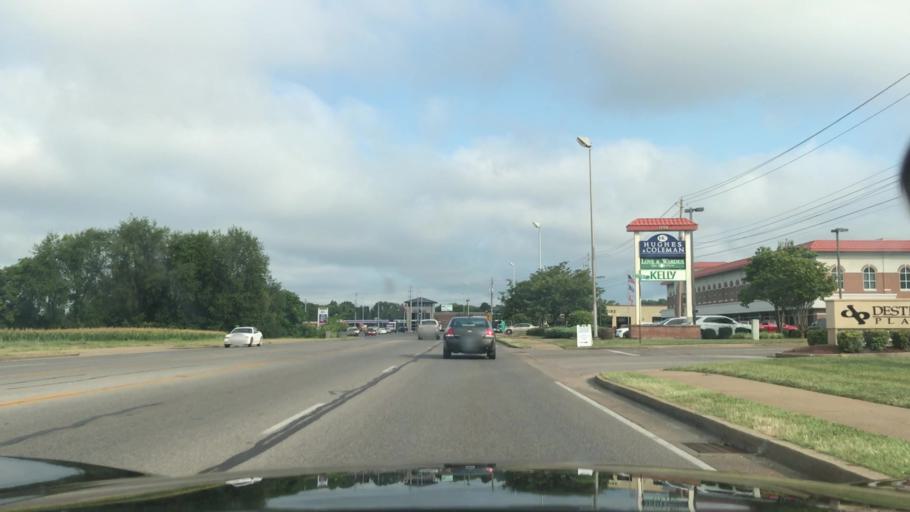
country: US
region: Kentucky
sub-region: Warren County
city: Bowling Green
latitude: 36.9588
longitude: -86.4496
